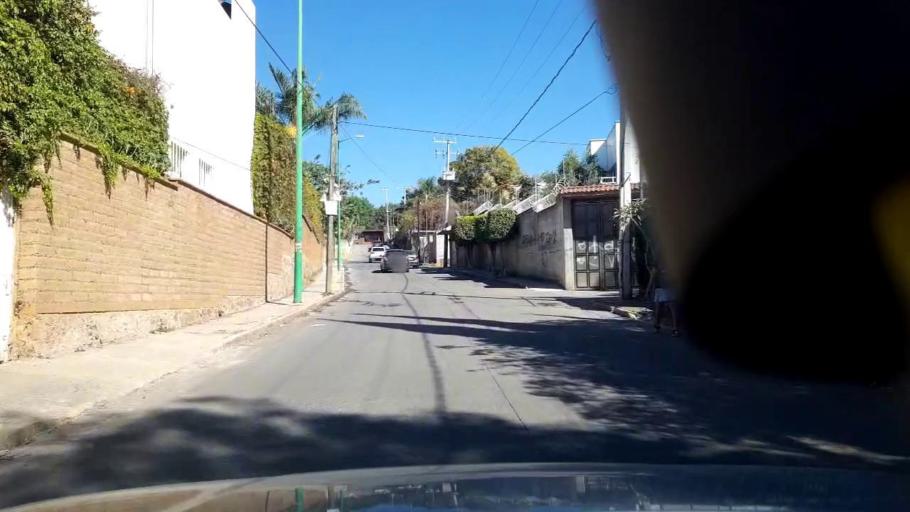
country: MX
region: Morelos
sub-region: Cuernavaca
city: Colonia los Cerritos
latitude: 18.9659
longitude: -99.2228
